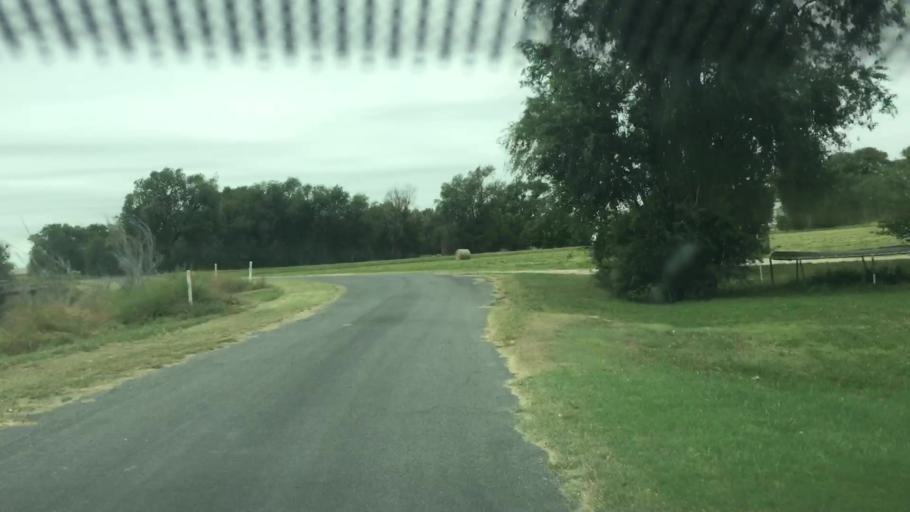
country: US
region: Kansas
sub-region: Hamilton County
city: Syracuse
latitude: 38.0572
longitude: -102.1171
